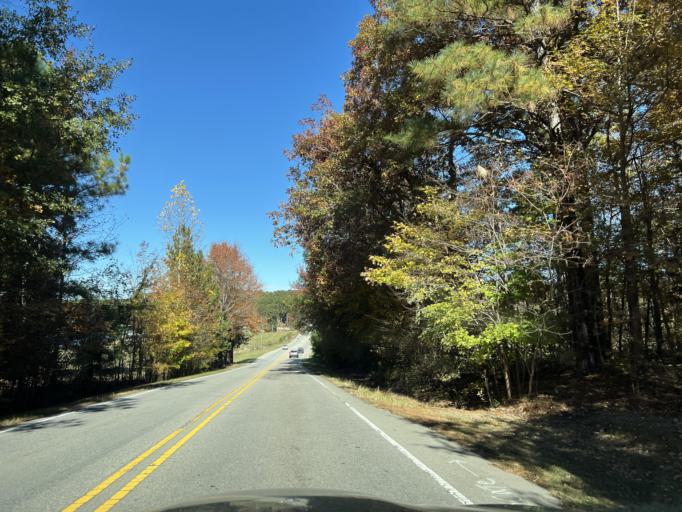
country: US
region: North Carolina
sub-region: Wake County
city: Garner
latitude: 35.6903
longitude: -78.6940
